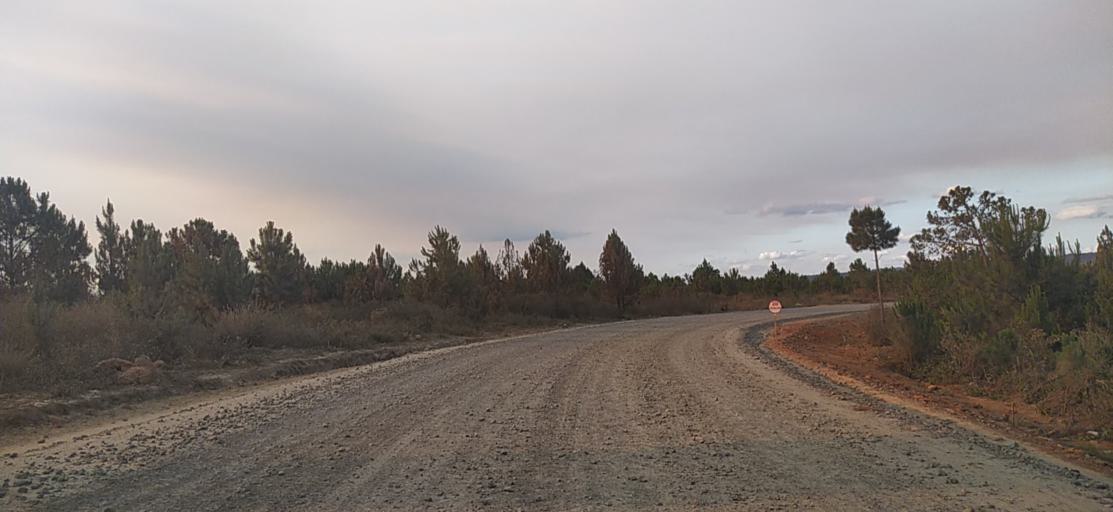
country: MG
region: Analamanga
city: Anjozorobe
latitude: -18.5085
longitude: 48.2620
